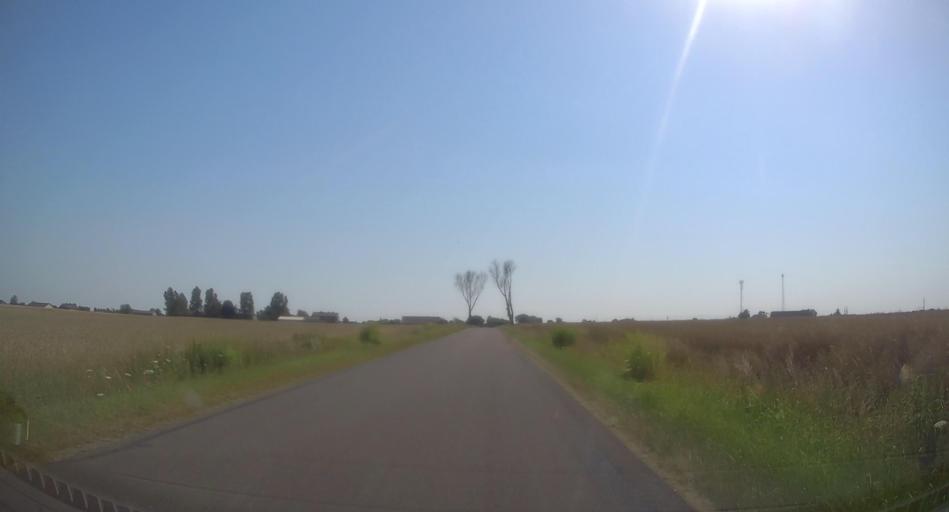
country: PL
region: Lodz Voivodeship
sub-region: Powiat skierniewicki
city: Kaweczyn Nowy
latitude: 51.8823
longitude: 20.2197
